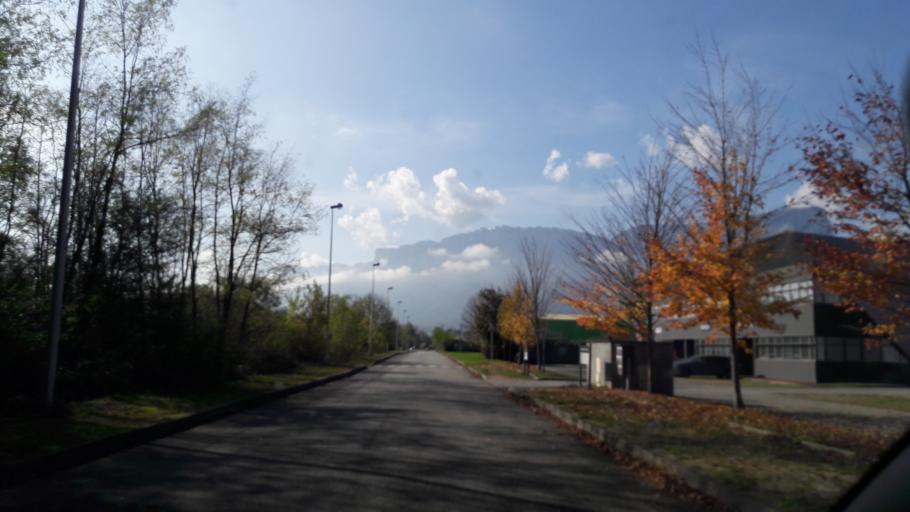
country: FR
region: Rhone-Alpes
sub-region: Departement de la Savoie
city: Montmelian
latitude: 45.4804
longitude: 6.0403
